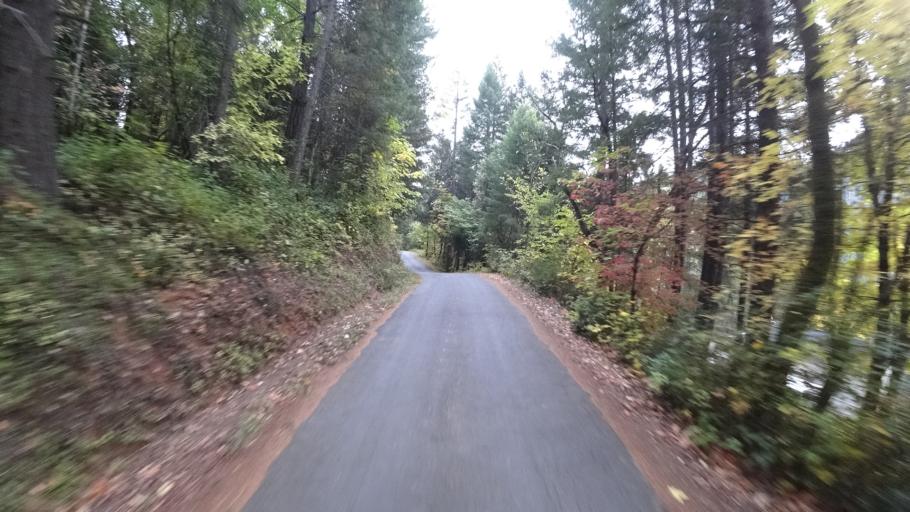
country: US
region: California
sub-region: Siskiyou County
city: Happy Camp
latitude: 41.7947
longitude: -123.3435
